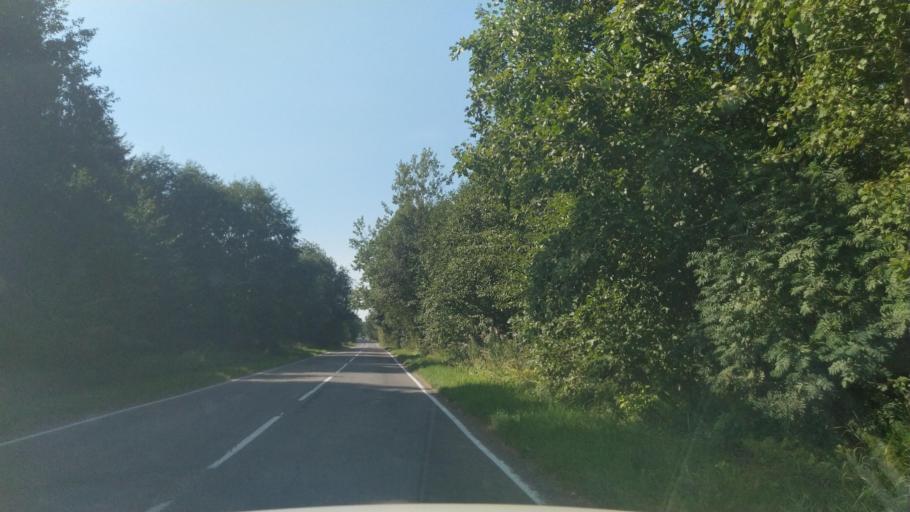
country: RU
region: Leningrad
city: Siverskiy
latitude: 59.3023
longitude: 30.0792
